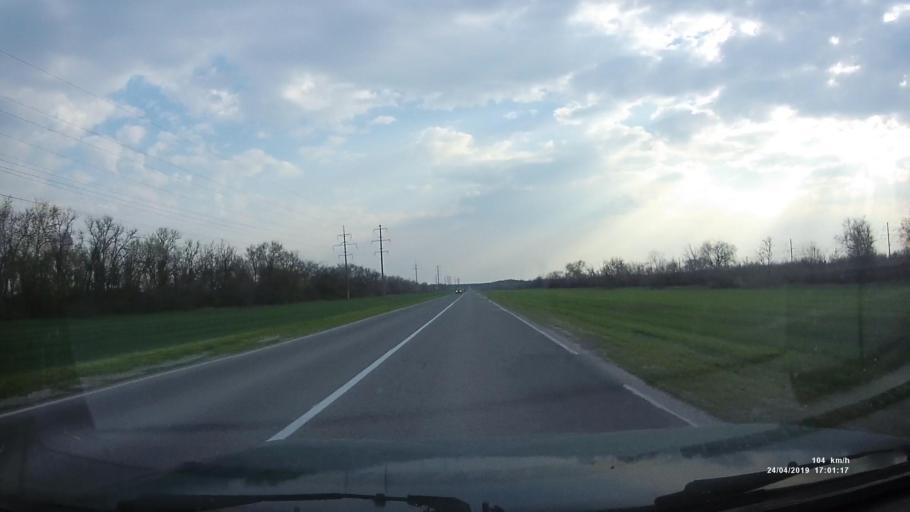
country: RU
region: Rostov
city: Proletarsk
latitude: 46.5947
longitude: 41.6269
